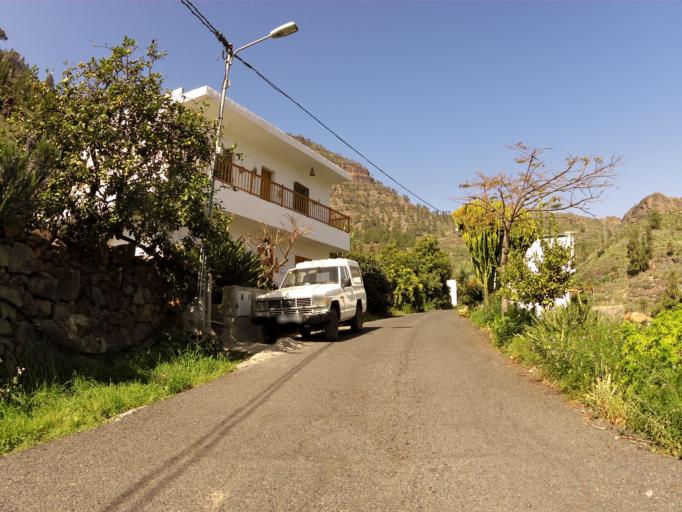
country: ES
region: Canary Islands
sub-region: Provincia de Las Palmas
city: Mogan
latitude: 27.8947
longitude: -15.6775
